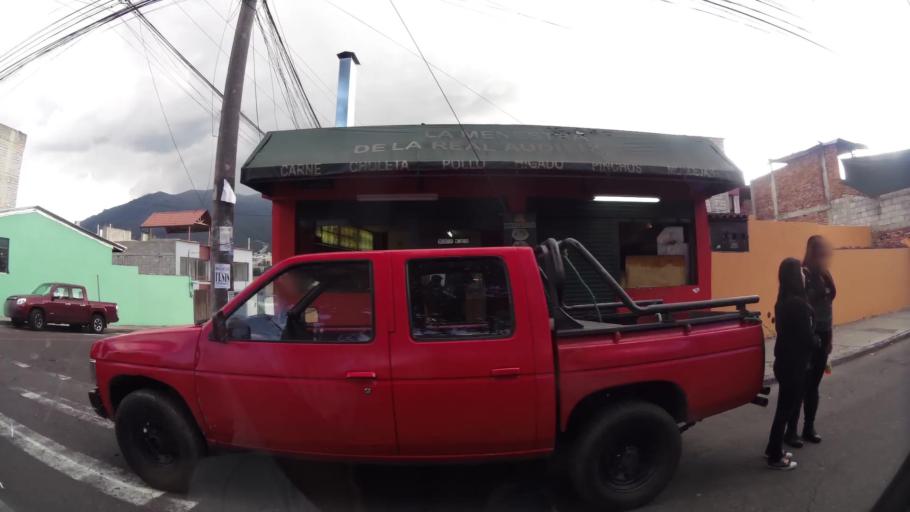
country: EC
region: Pichincha
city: Quito
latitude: -0.1306
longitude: -78.4873
